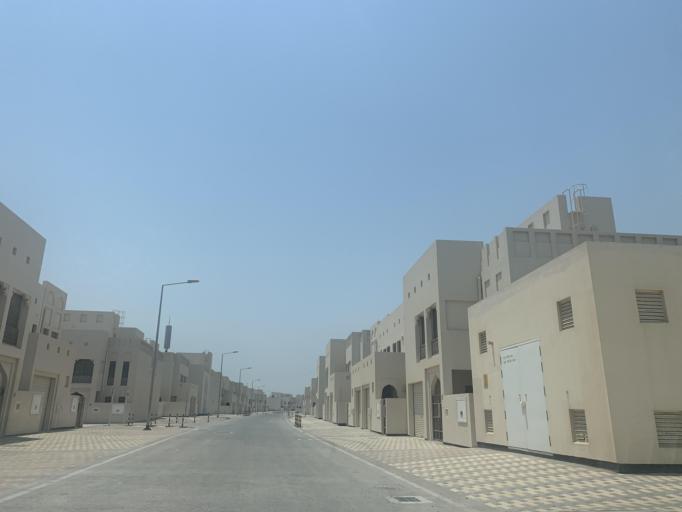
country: BH
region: Muharraq
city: Al Hadd
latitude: 26.2409
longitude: 50.6717
